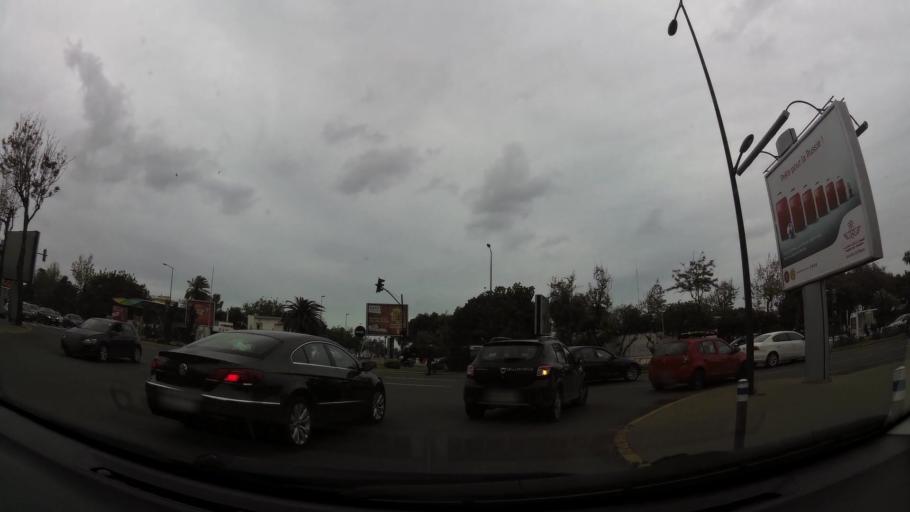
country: MA
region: Grand Casablanca
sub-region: Casablanca
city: Casablanca
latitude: 33.5903
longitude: -7.6539
